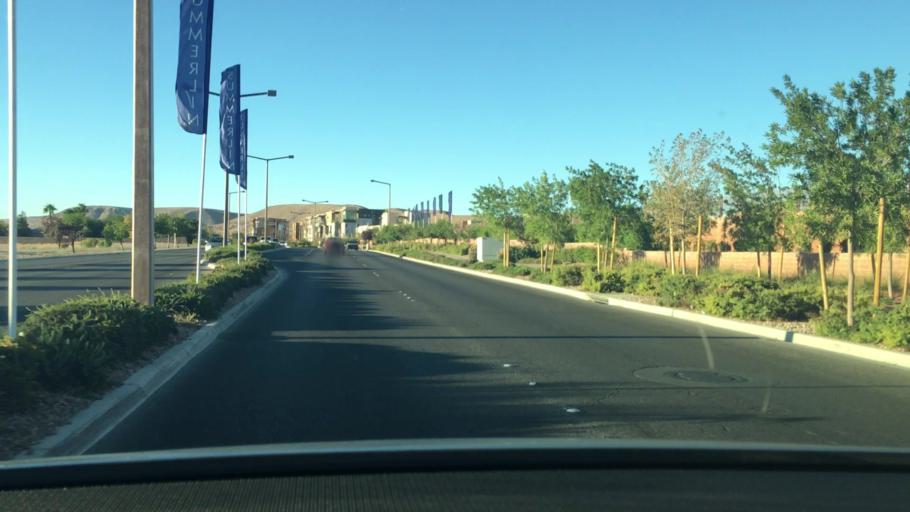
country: US
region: Nevada
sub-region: Clark County
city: Summerlin South
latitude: 36.1149
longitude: -115.3296
